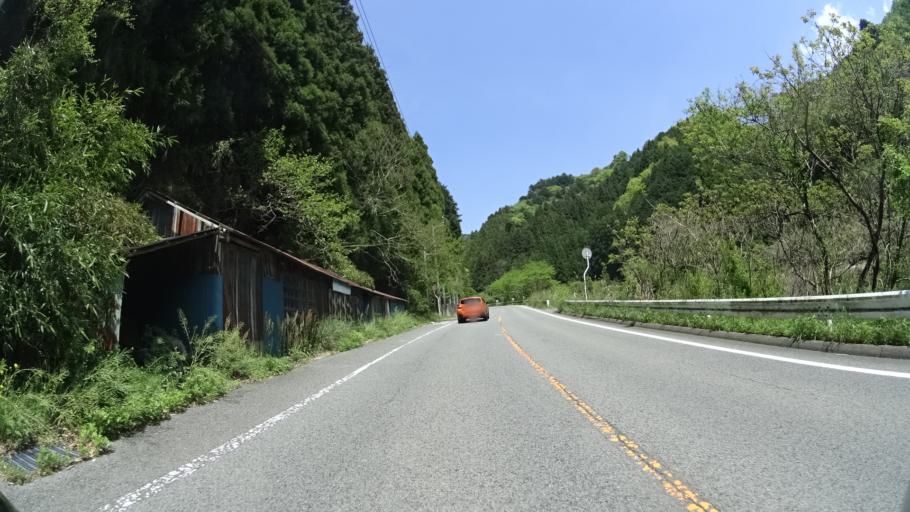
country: JP
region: Ehime
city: Hojo
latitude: 33.9281
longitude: 132.8932
